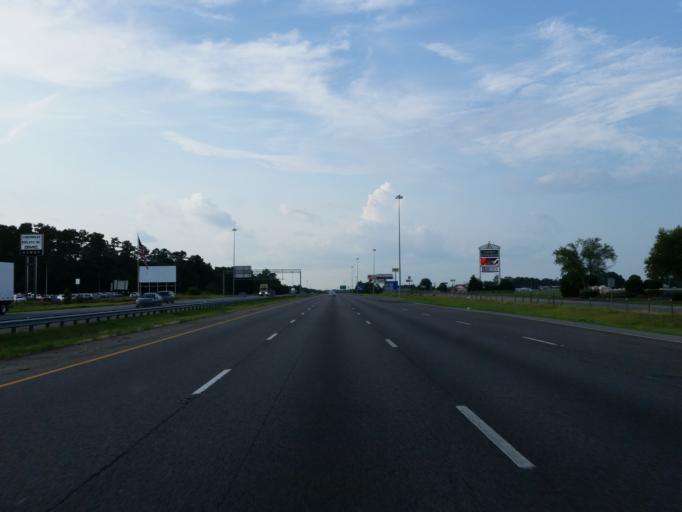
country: US
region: Georgia
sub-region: Houston County
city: Perry
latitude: 32.4370
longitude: -83.7560
